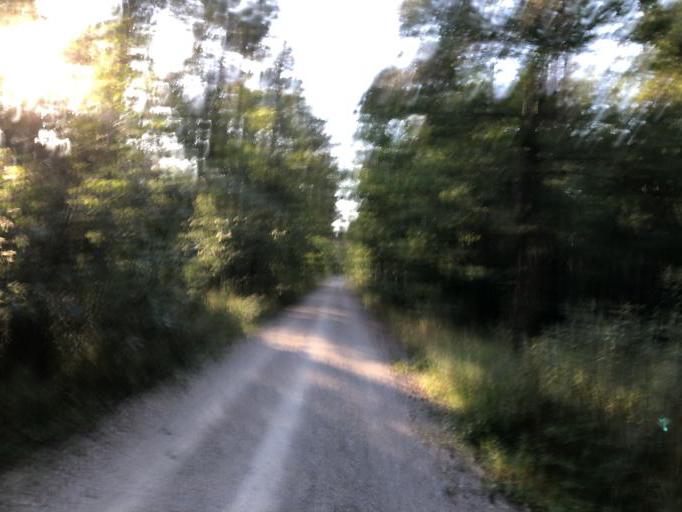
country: DE
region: Bavaria
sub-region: Regierungsbezirk Mittelfranken
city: Uttenreuth
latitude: 49.5849
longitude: 11.0654
